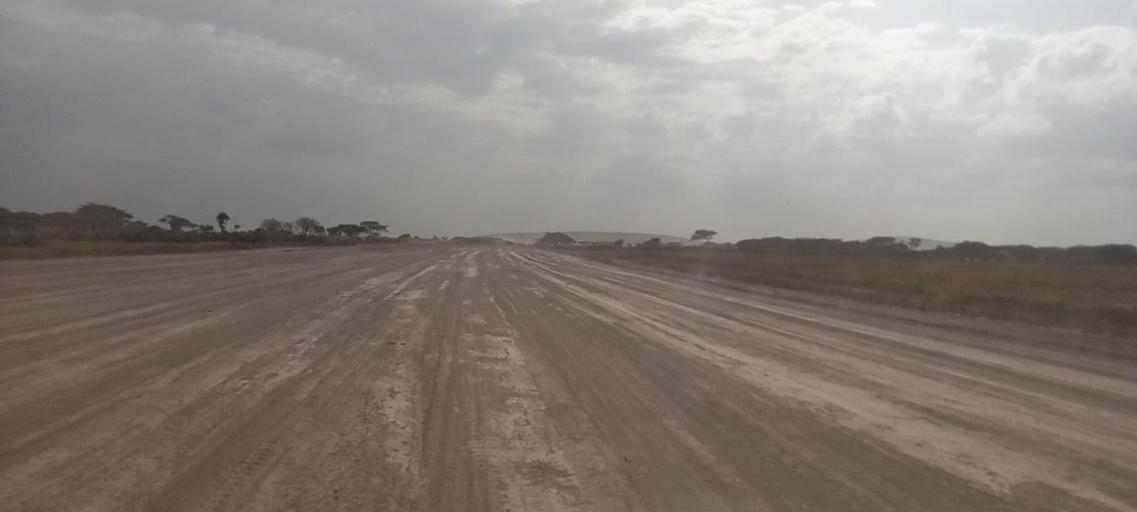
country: ET
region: Oromiya
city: Ziway
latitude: 7.8525
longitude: 38.6645
